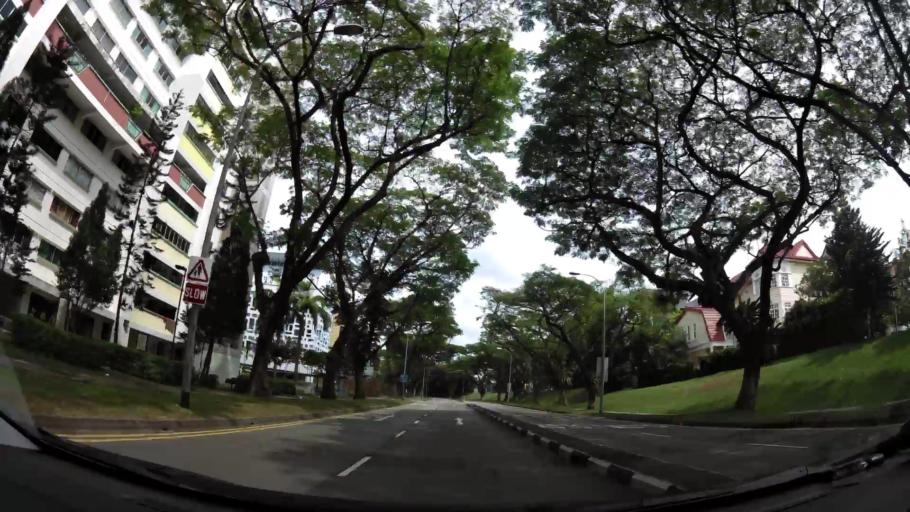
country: MY
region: Johor
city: Johor Bahru
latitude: 1.4292
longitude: 103.7788
